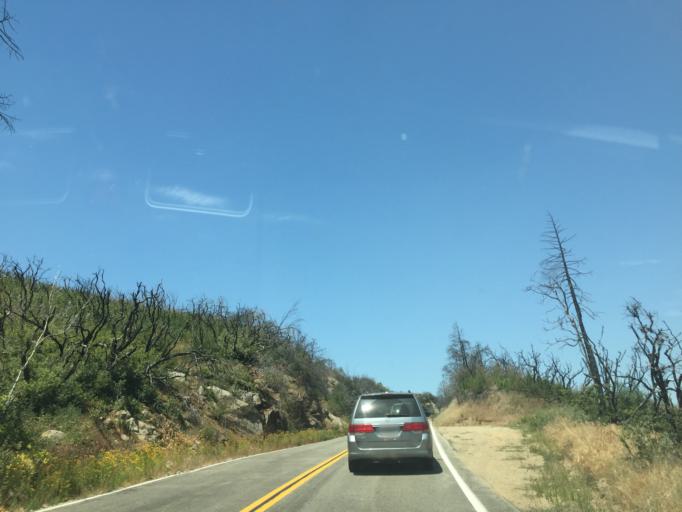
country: US
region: California
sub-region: Fresno County
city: Squaw Valley
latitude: 36.8300
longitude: -118.9029
